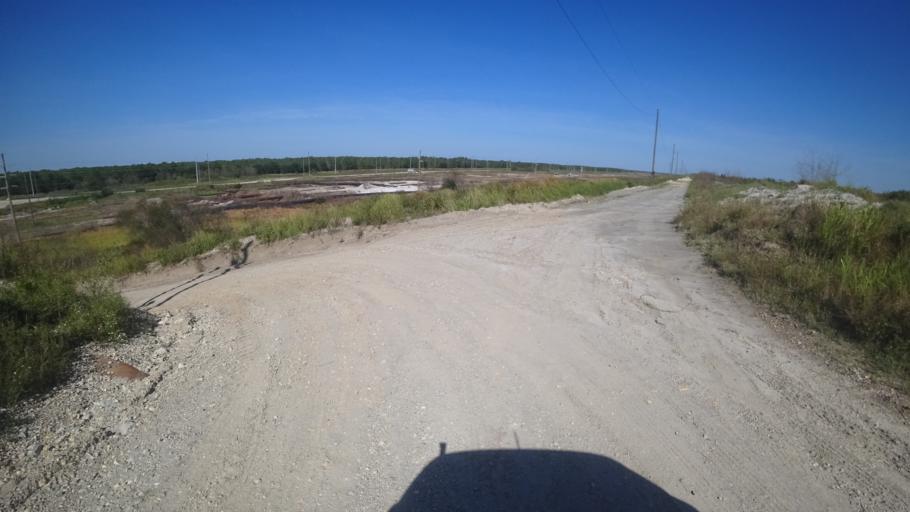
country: US
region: Florida
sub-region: Hillsborough County
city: Balm
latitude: 27.6495
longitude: -82.0890
